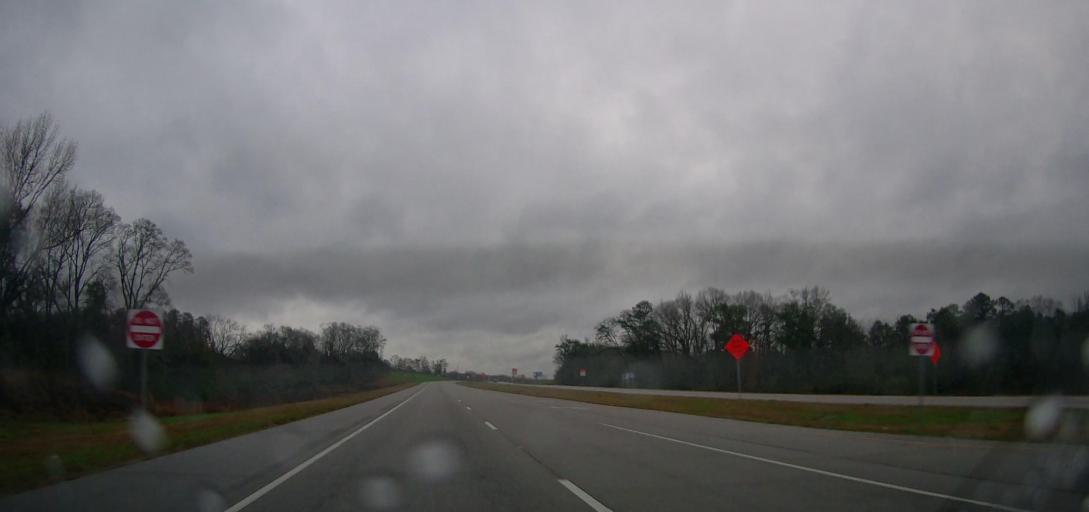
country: US
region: Alabama
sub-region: Bibb County
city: Centreville
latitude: 32.9403
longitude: -87.0716
